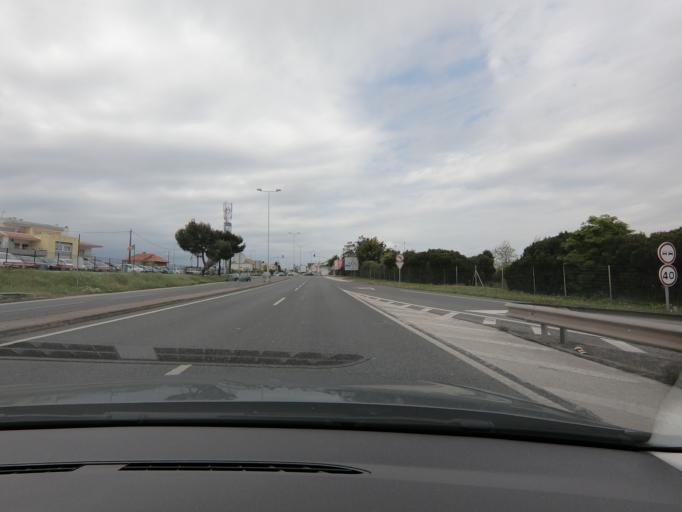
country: PT
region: Lisbon
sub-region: Cascais
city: Sao Domingos de Rana
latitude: 38.7092
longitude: -9.3386
